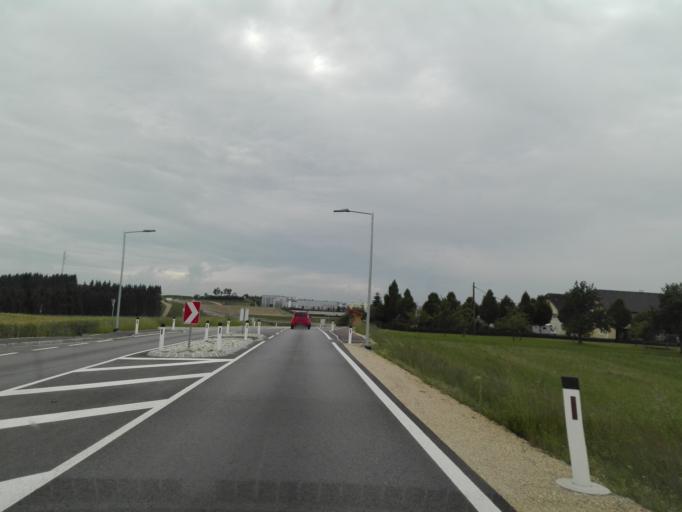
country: AT
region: Upper Austria
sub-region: Politischer Bezirk Perg
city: Bad Kreuzen
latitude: 48.2777
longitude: 14.7219
